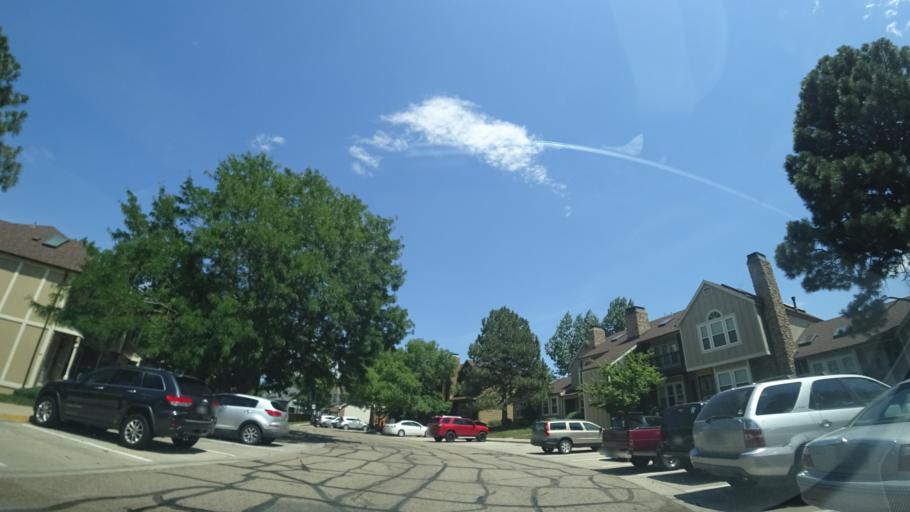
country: US
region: Colorado
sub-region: Jefferson County
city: Lakewood
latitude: 39.6940
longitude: -105.0987
